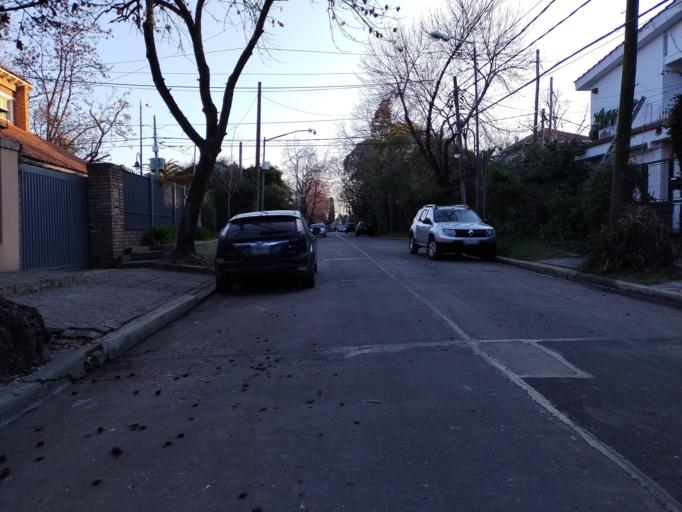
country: AR
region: Buenos Aires
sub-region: Partido de San Isidro
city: San Isidro
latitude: -34.4473
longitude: -58.5361
